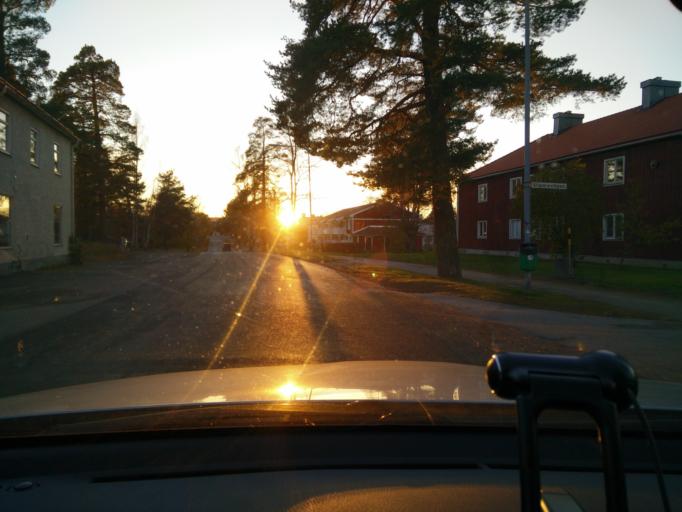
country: SE
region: Vaesternorrland
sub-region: Sundsvalls Kommun
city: Matfors
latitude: 62.3502
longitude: 17.0361
